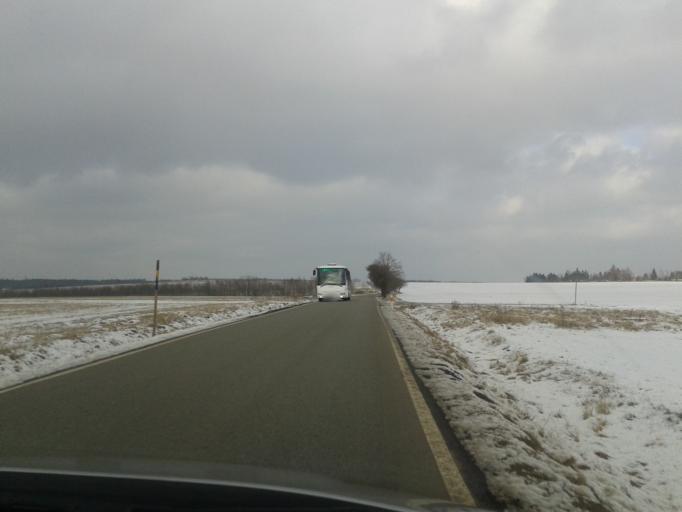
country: CZ
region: Olomoucky
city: Horni Stepanov
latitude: 49.5730
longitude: 16.8237
